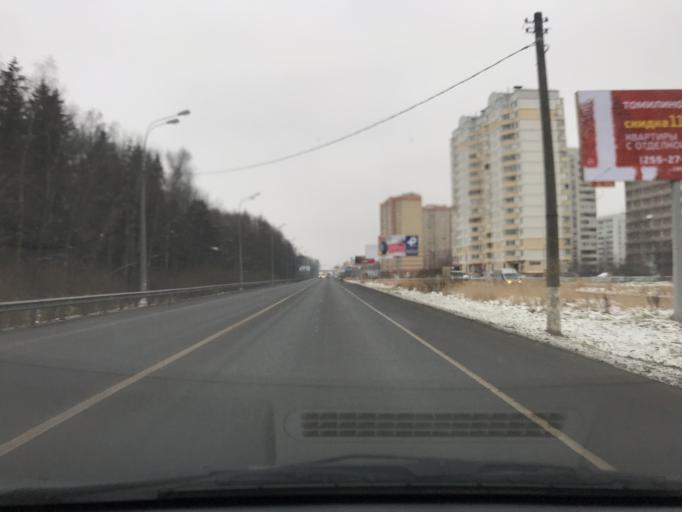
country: RU
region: Moskovskaya
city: Elektrostal'
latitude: 55.7996
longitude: 38.4289
